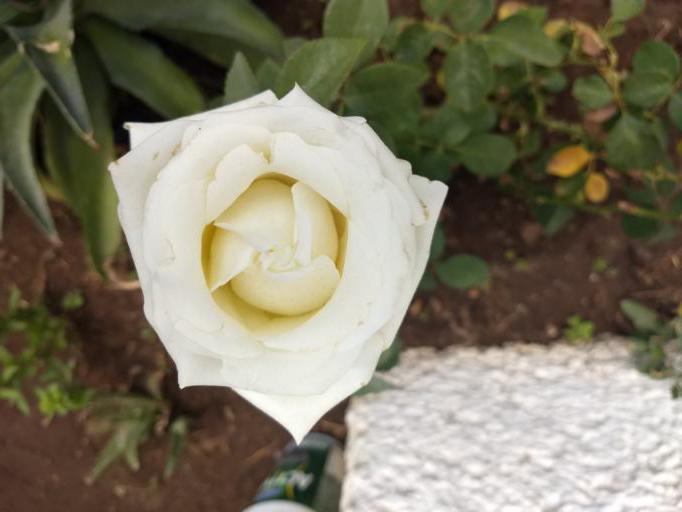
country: MX
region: Michoacan
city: Maravatio
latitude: 19.9090
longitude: -100.4545
